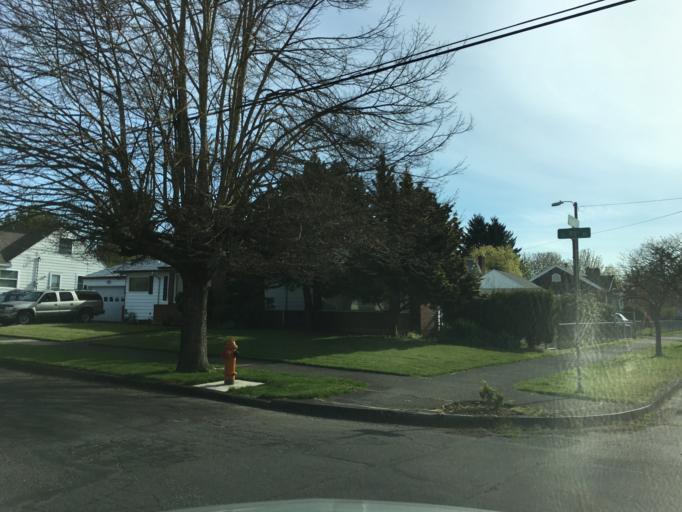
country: US
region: Oregon
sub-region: Multnomah County
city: Lents
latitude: 45.5211
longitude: -122.5761
